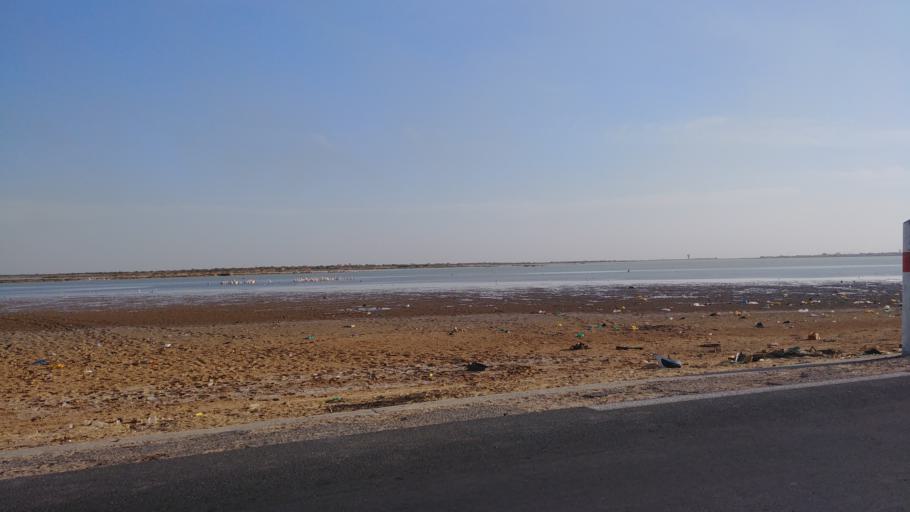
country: SN
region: Saint-Louis
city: Saint-Louis
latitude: 16.0253
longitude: -16.4791
